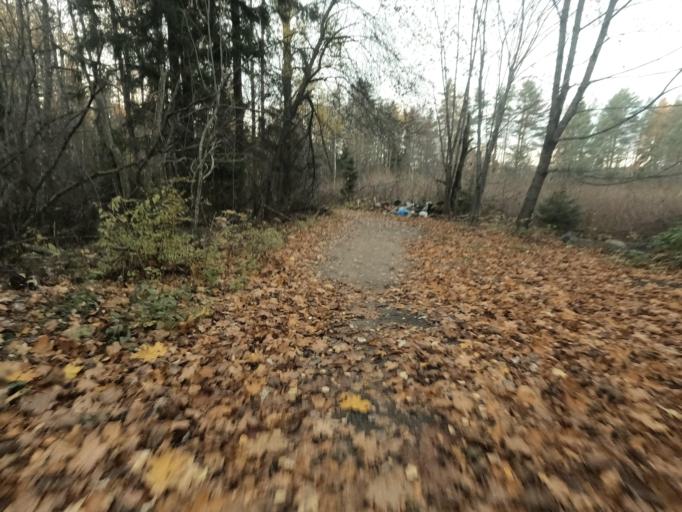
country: RU
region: Leningrad
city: Leninskoye
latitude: 60.1949
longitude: 29.8550
